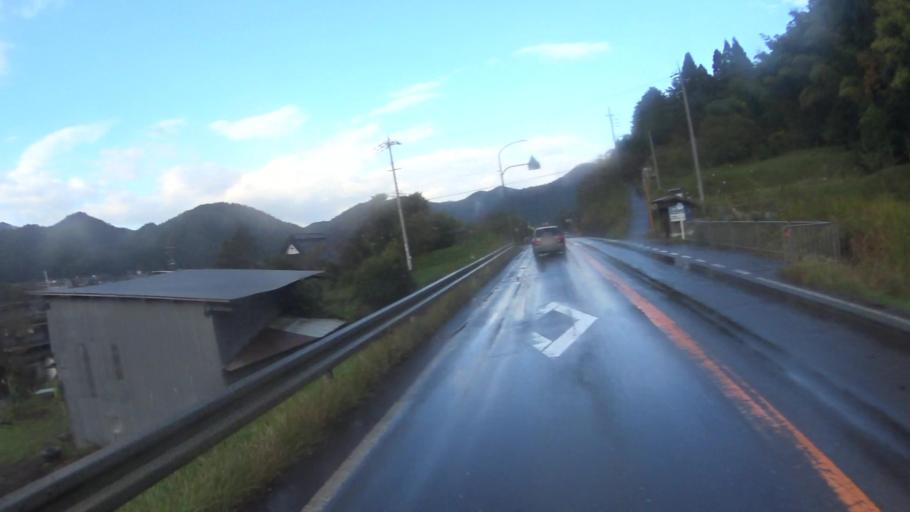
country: JP
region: Kyoto
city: Ayabe
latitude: 35.2002
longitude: 135.2540
